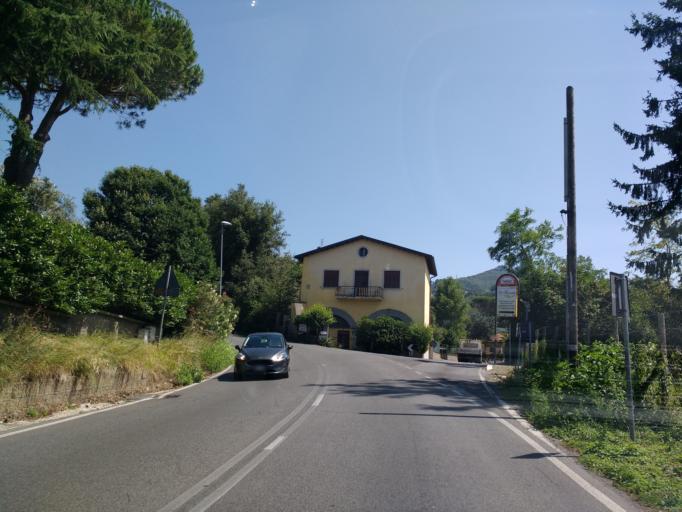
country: IT
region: Latium
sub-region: Citta metropolitana di Roma Capitale
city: Rocca di Papa
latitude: 41.7729
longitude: 12.6999
